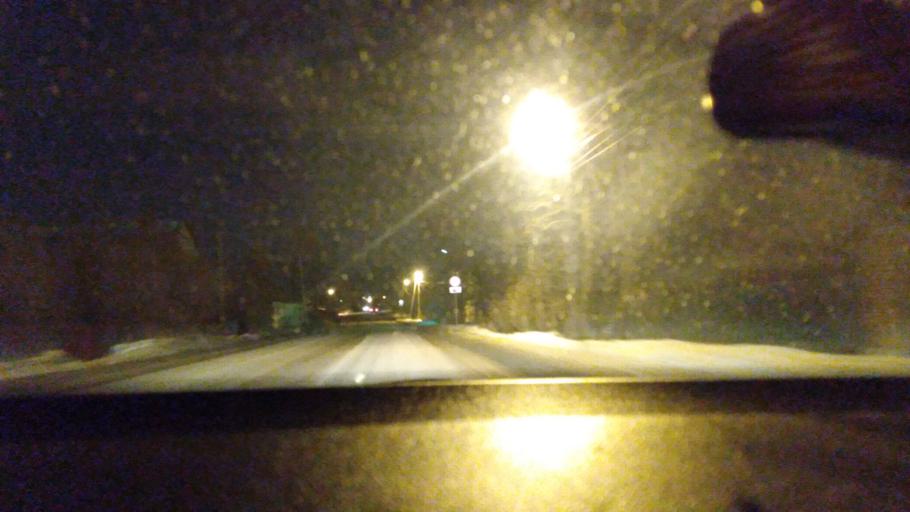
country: RU
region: Moskovskaya
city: Chornaya
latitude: 55.7058
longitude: 38.0511
